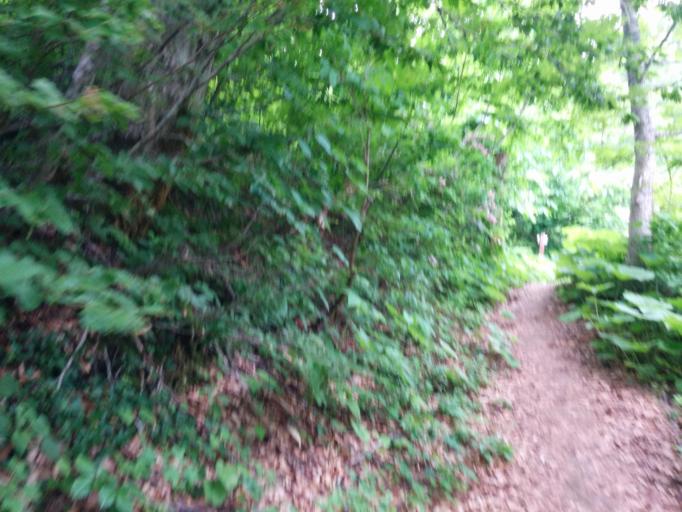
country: JP
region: Aomori
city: Hirosaki
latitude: 40.5560
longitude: 140.1639
